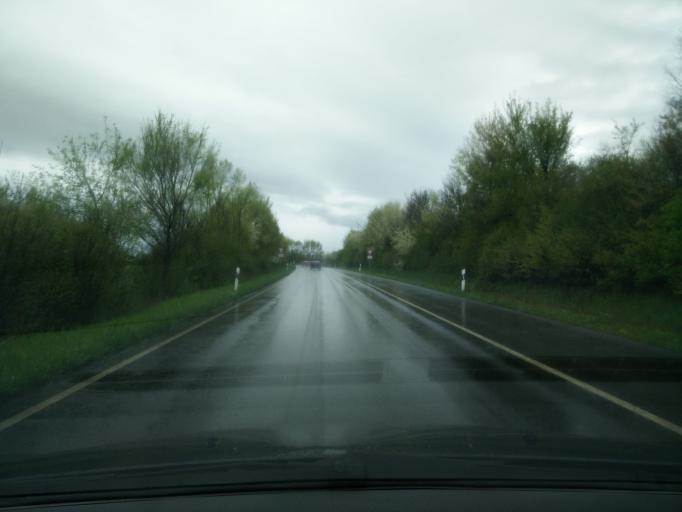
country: DE
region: Rheinland-Pfalz
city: Impflingen
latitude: 49.1741
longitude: 8.1171
